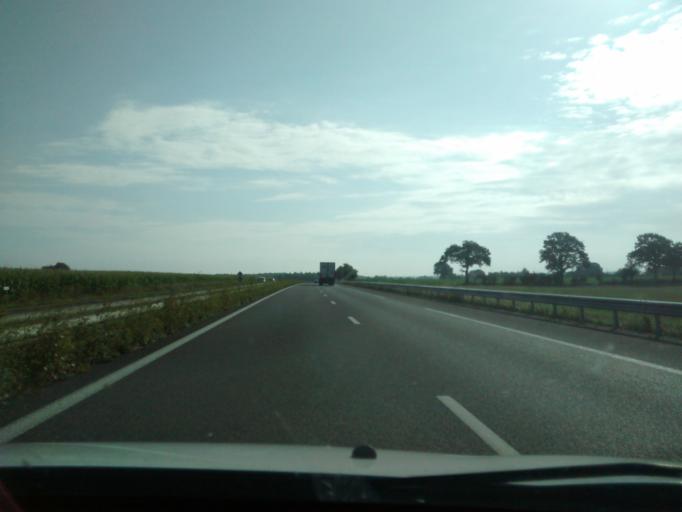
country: FR
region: Brittany
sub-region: Departement d'Ille-et-Vilaine
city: Erbree
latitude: 48.0862
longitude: -1.1192
